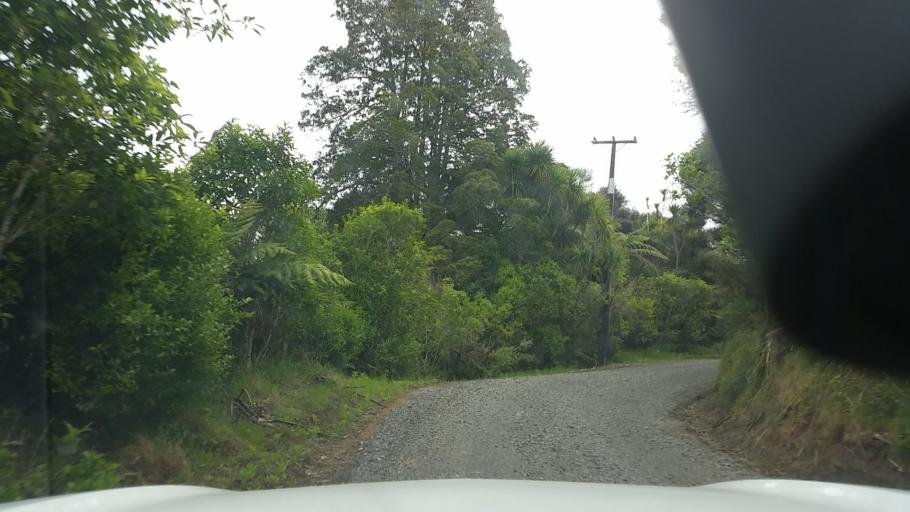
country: NZ
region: Auckland
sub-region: Auckland
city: Muriwai Beach
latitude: -36.8749
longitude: 174.5092
